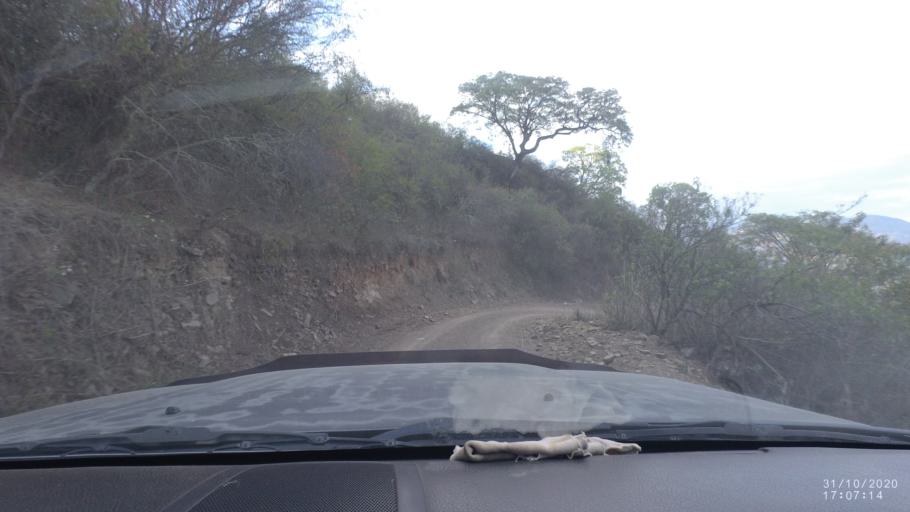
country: BO
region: Chuquisaca
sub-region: Provincia Zudanez
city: Mojocoya
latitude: -18.5452
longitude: -64.5433
